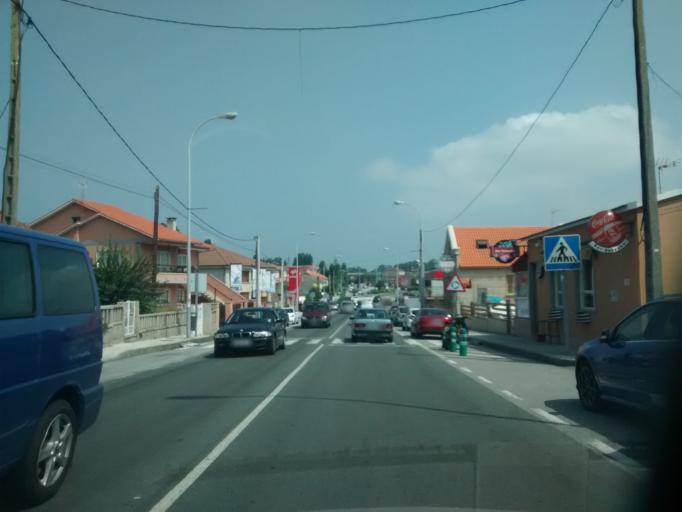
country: ES
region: Galicia
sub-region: Provincia de Pontevedra
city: Sanxenxo
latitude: 42.4102
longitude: -8.8132
